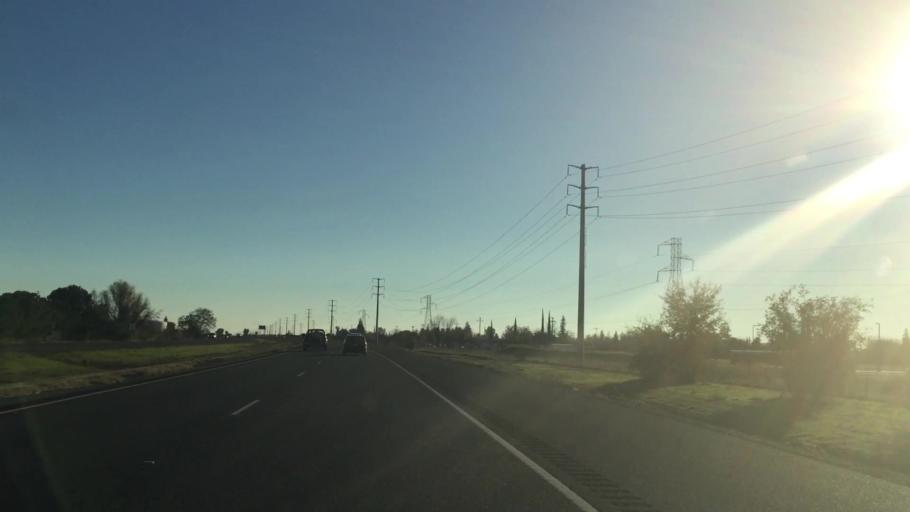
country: US
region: California
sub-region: Yuba County
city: Olivehurst
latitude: 39.0877
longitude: -121.5424
